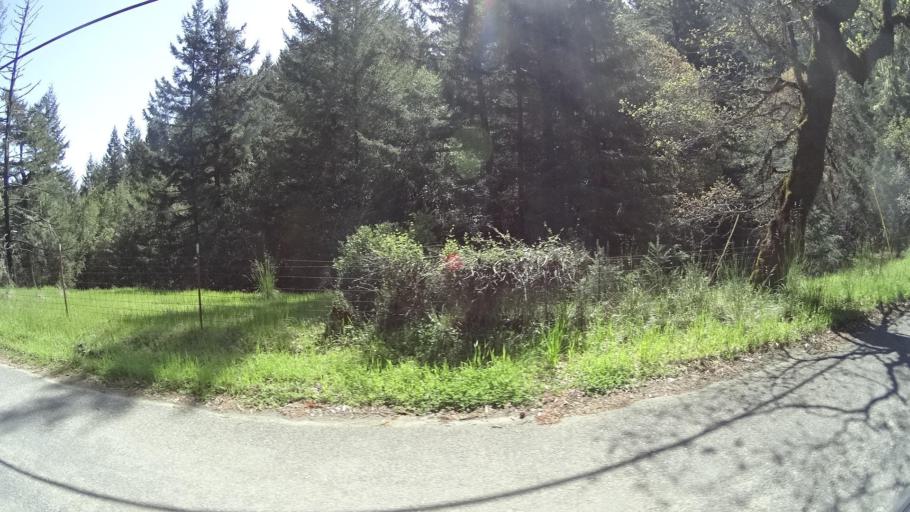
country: US
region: California
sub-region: Humboldt County
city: Redway
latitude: 40.0456
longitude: -123.6425
